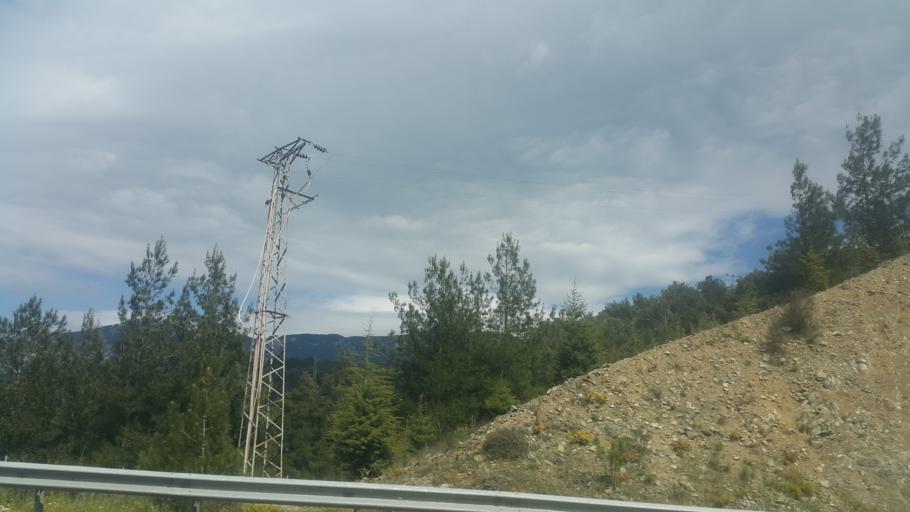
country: TR
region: Adana
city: Pozanti
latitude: 37.4419
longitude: 34.8832
